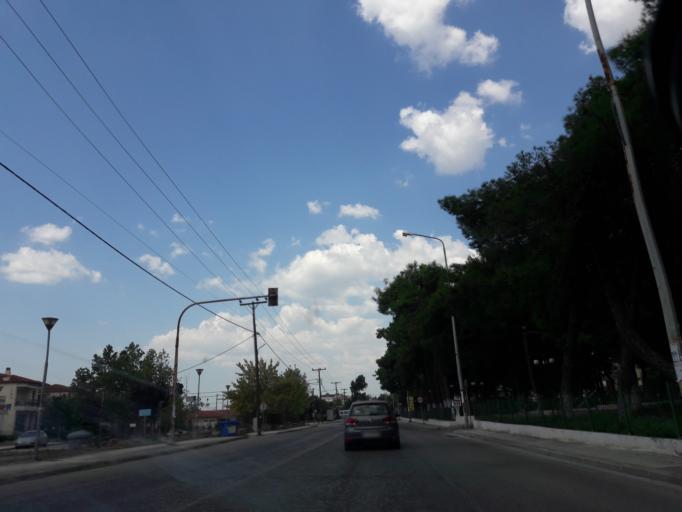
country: GR
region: Central Macedonia
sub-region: Nomos Thessalonikis
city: Thermi
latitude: 40.5250
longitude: 23.0493
